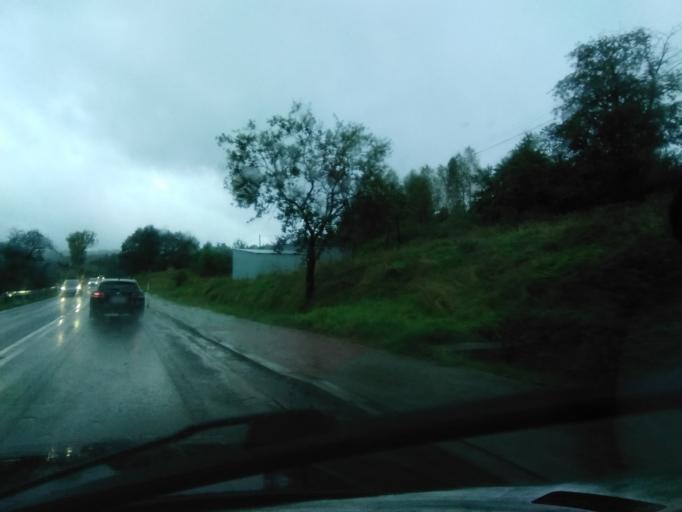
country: PL
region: Subcarpathian Voivodeship
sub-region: Powiat ropczycko-sedziszowski
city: Niedzwiada
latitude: 50.0147
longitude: 21.5515
